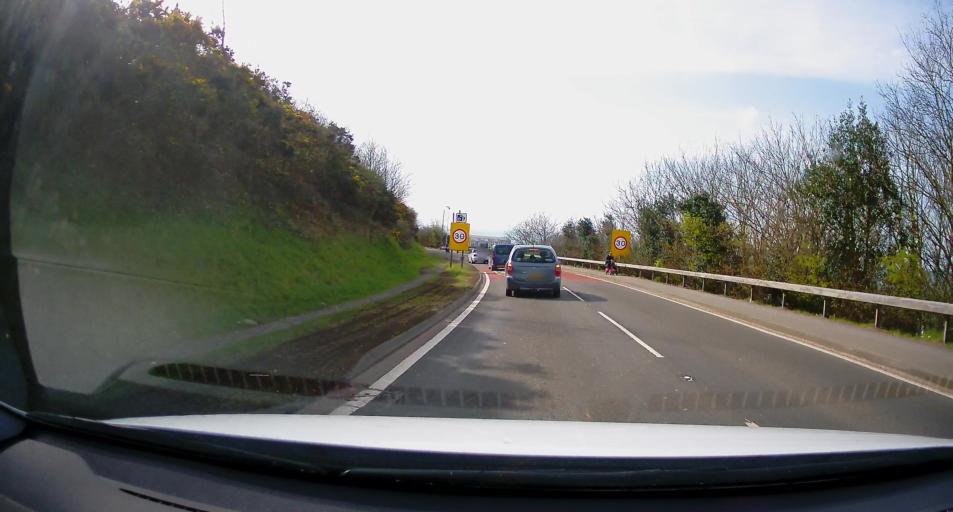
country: GB
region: Wales
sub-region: County of Ceredigion
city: Aberaeron
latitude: 52.2452
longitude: -4.2515
